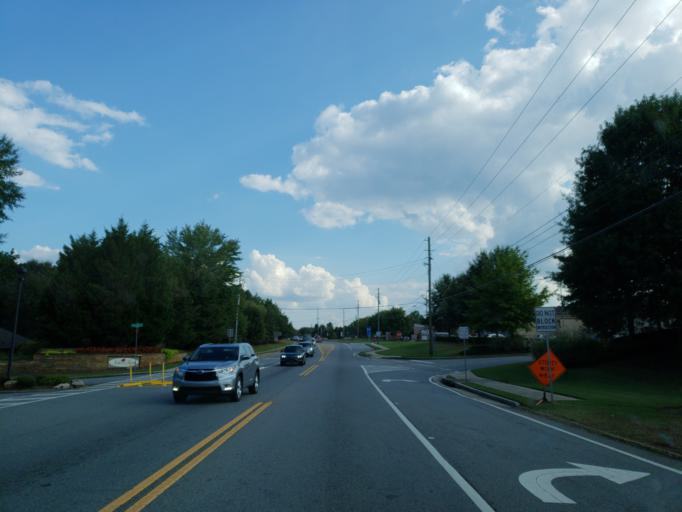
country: US
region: Georgia
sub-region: Fulton County
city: Roswell
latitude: 34.0803
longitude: -84.3566
